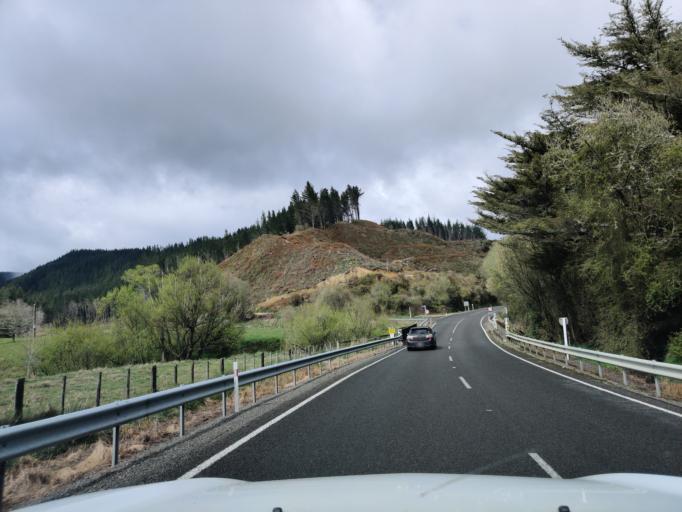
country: NZ
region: Waikato
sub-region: Otorohanga District
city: Otorohanga
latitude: -38.6148
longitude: 175.2195
